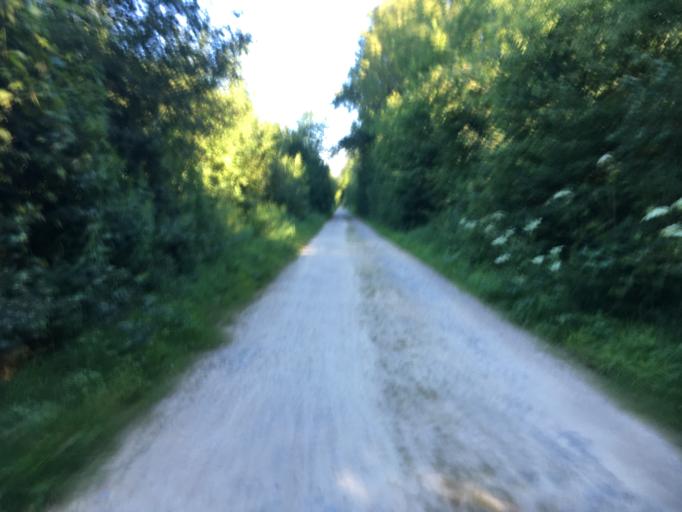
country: CH
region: Fribourg
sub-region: See District
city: Bas-Vully
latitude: 46.9501
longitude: 7.1319
